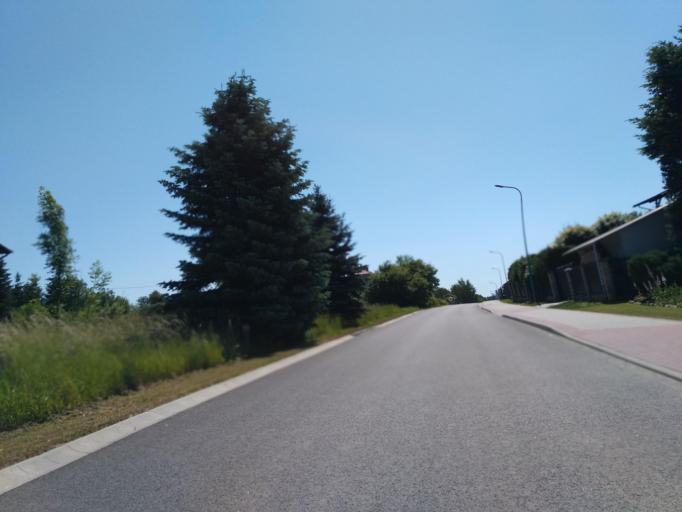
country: PL
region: Subcarpathian Voivodeship
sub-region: Powiat krosnienski
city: Korczyna
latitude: 49.7195
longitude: 21.8004
